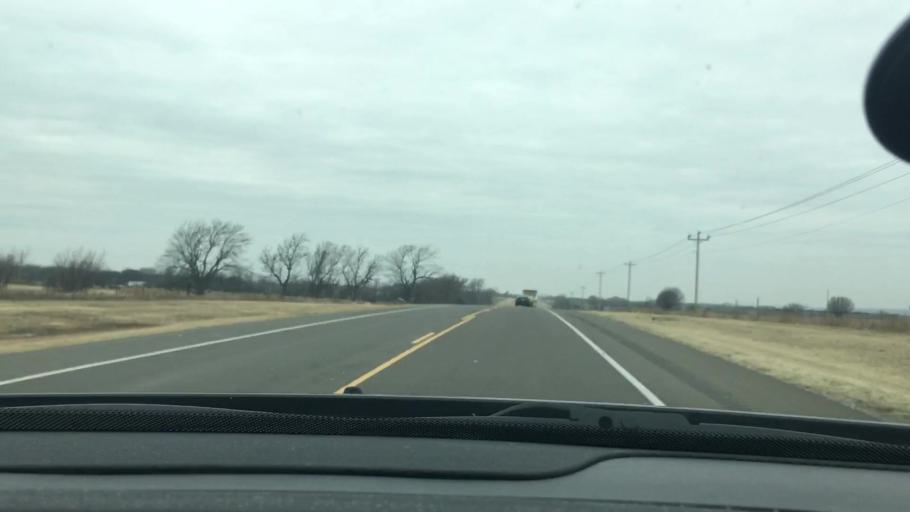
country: US
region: Oklahoma
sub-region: Murray County
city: Davis
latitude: 34.5213
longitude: -97.2273
